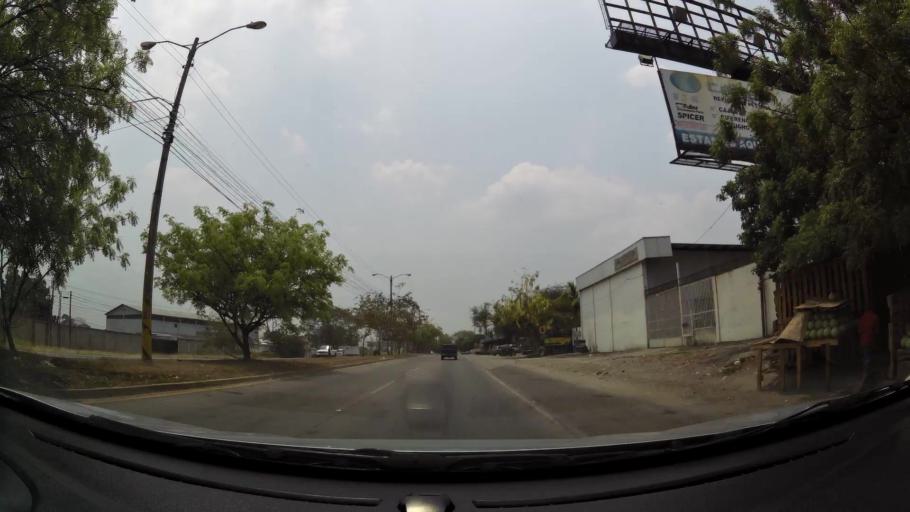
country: HN
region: Cortes
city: La Lima
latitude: 15.4622
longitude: -87.9592
